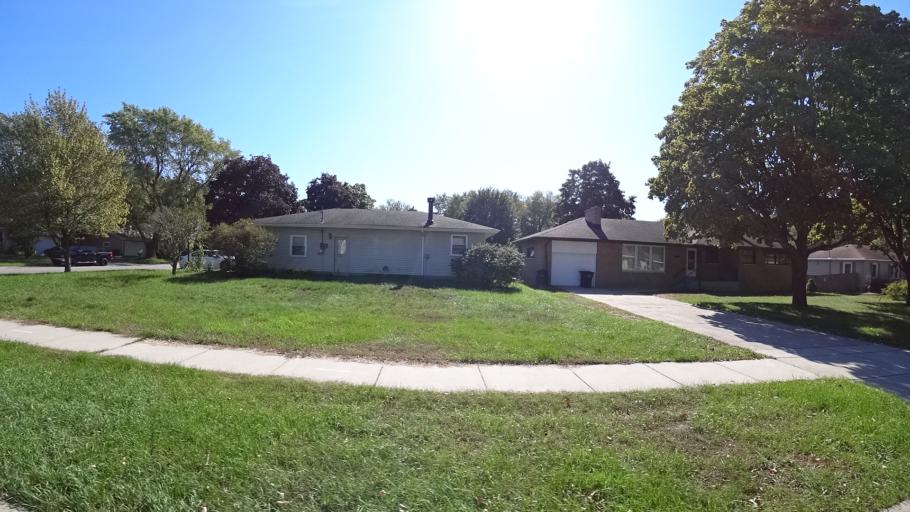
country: US
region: Indiana
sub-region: LaPorte County
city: Michigan City
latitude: 41.6948
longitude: -86.8834
